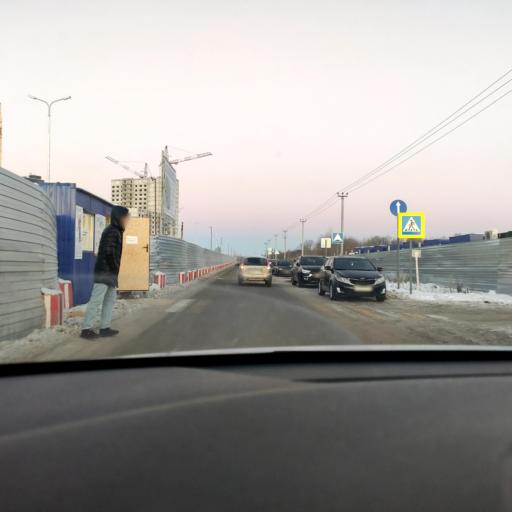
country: RU
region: Tatarstan
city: Osinovo
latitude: 55.8587
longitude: 48.9091
